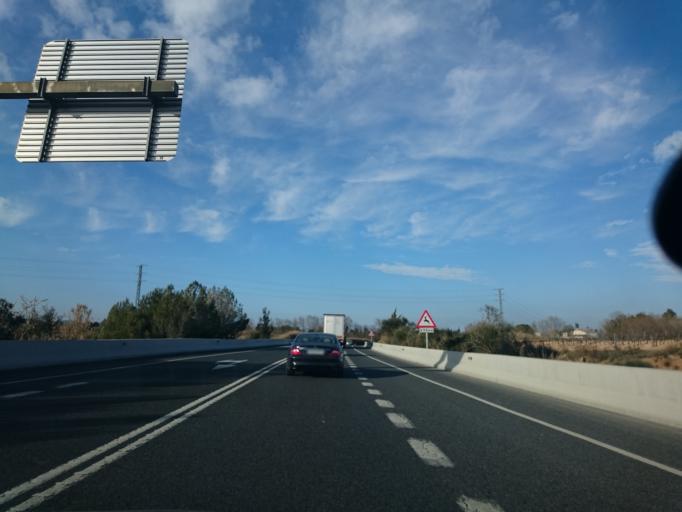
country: ES
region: Catalonia
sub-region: Provincia de Barcelona
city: Castellet
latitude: 41.3152
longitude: 1.6407
